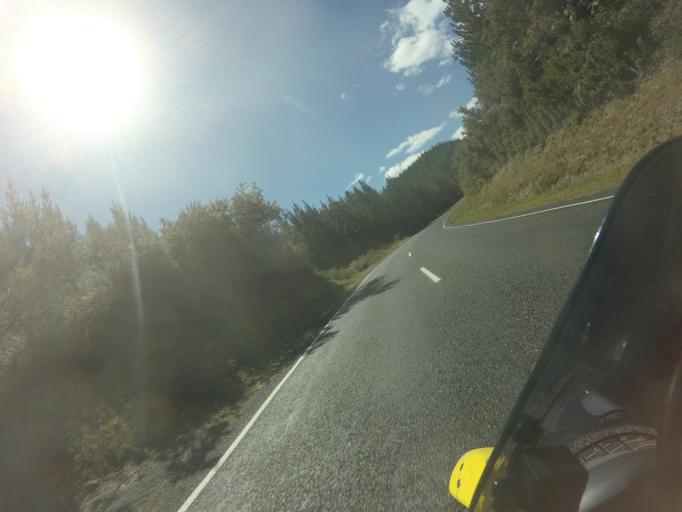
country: NZ
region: Bay of Plenty
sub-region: Whakatane District
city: Murupara
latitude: -38.2856
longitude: 176.8101
